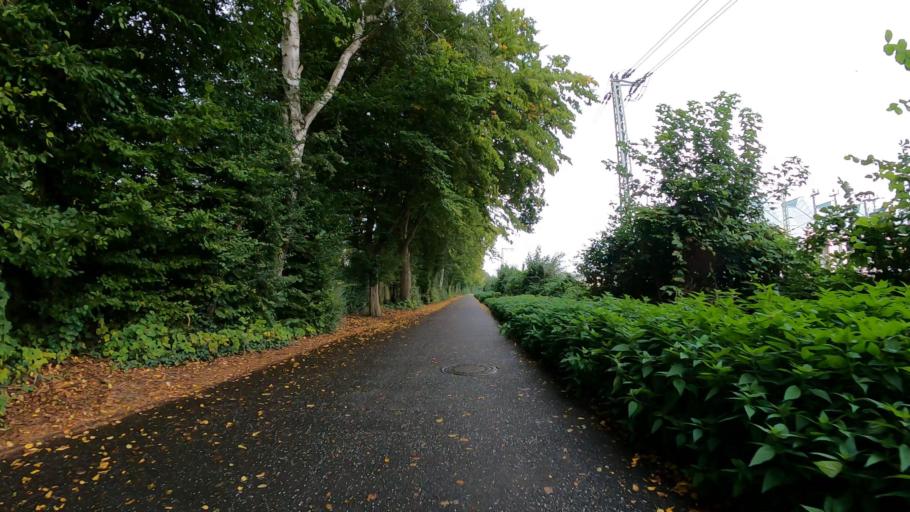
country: DE
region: Hamburg
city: Eidelstedt
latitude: 53.6048
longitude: 9.8838
